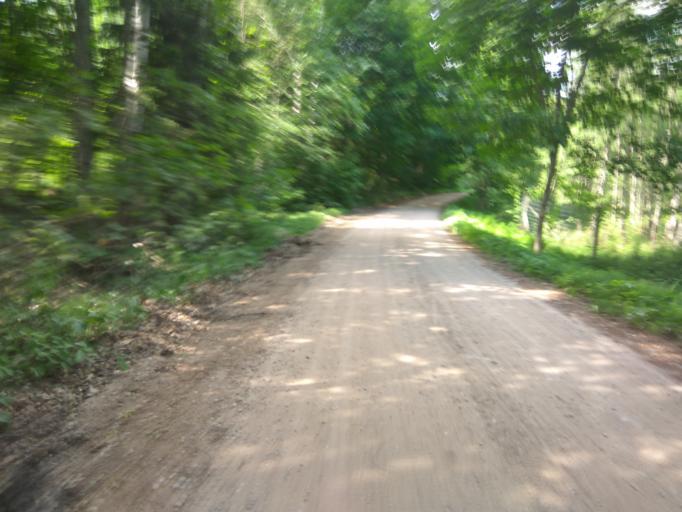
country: LV
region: Kuldigas Rajons
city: Kuldiga
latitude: 56.8850
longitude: 21.9281
